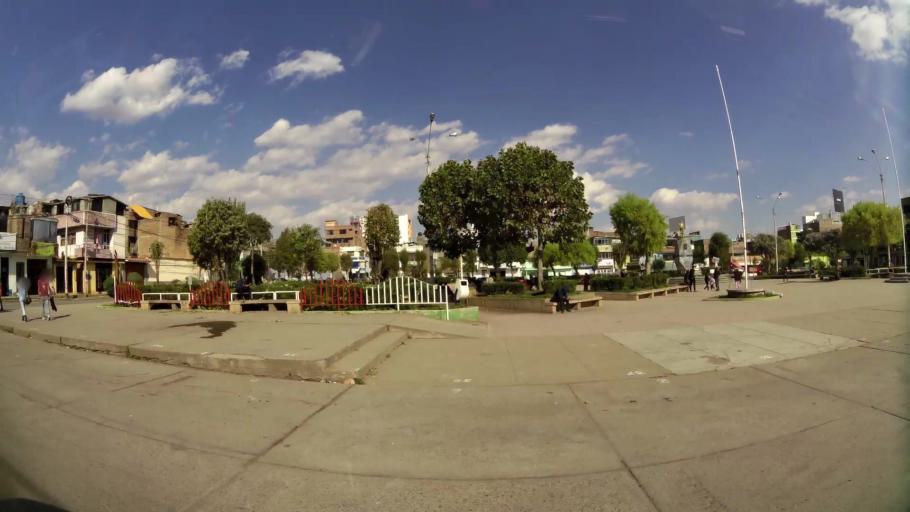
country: PE
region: Junin
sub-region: Provincia de Huancayo
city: El Tambo
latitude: -12.0633
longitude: -75.2172
